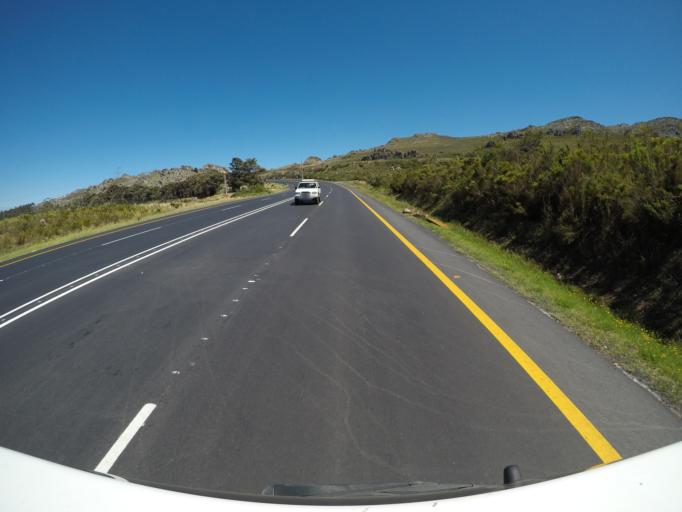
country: ZA
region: Western Cape
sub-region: Overberg District Municipality
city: Grabouw
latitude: -34.1506
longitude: 18.9353
